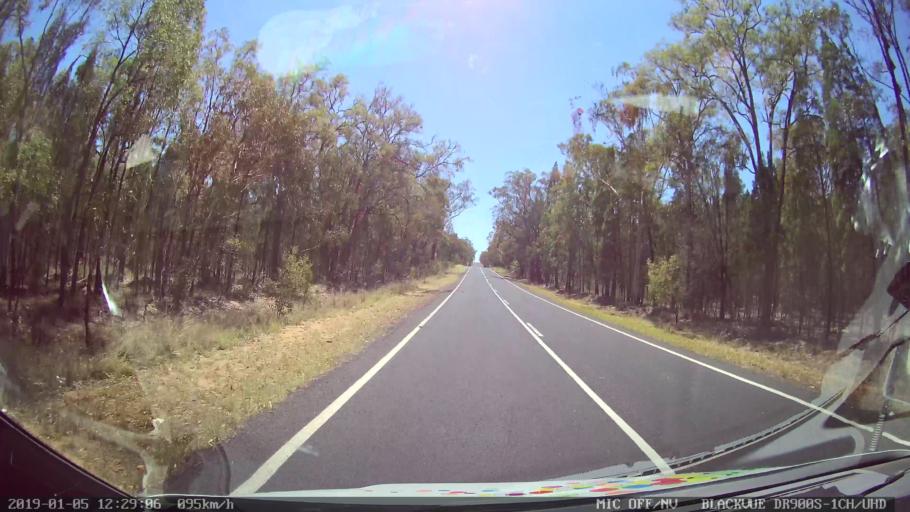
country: AU
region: New South Wales
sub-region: Warrumbungle Shire
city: Coonabarabran
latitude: -31.2356
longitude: 149.3325
